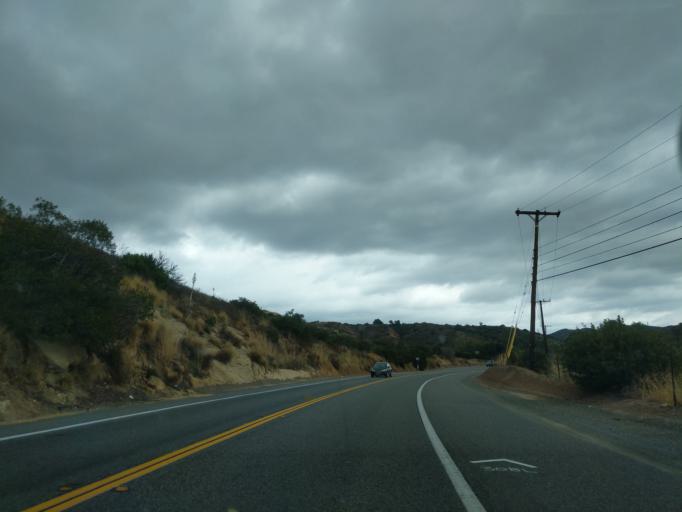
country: US
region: California
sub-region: Orange County
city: Foothill Ranch
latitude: 33.7475
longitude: -117.6700
